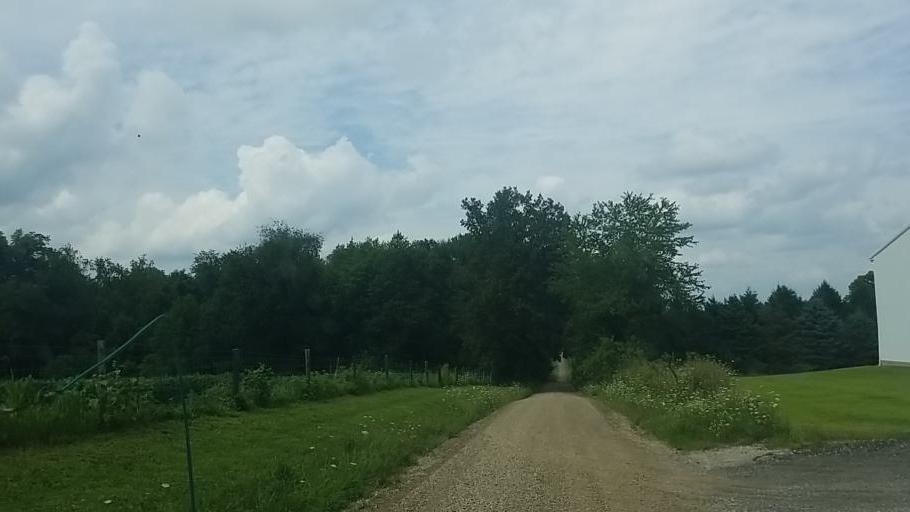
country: US
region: Ohio
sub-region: Knox County
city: Gambier
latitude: 40.3034
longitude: -82.3759
